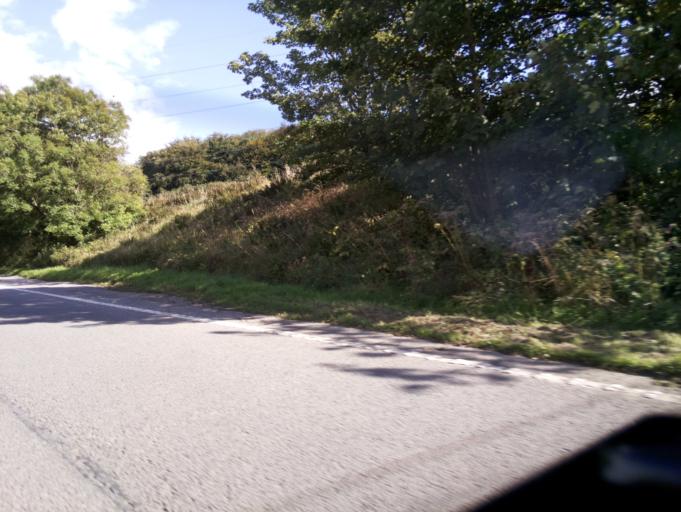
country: GB
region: England
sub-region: Devon
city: South Brent
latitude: 50.4311
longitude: -3.8017
